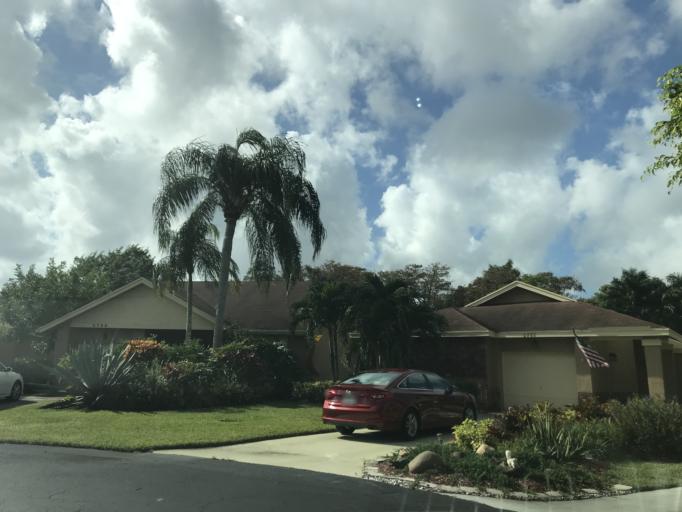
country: US
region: Florida
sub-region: Broward County
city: Coconut Creek
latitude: 26.2637
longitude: -80.1902
